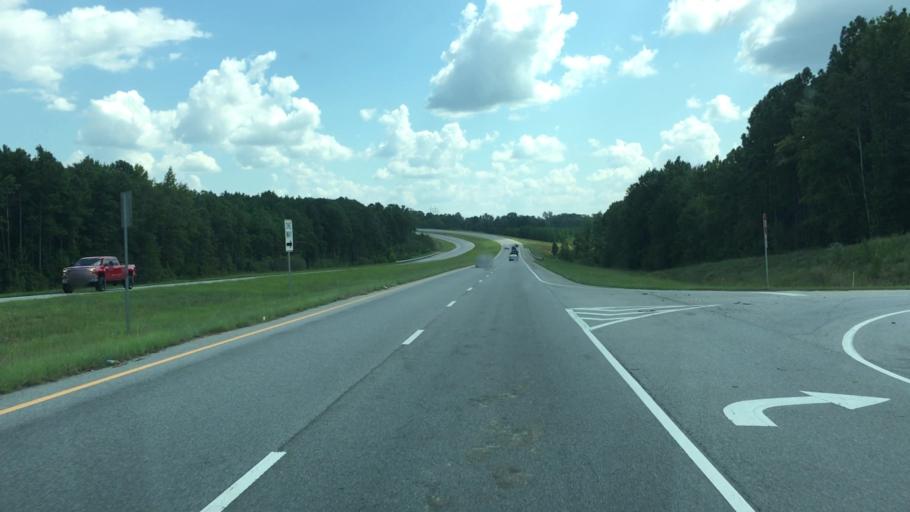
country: US
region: Georgia
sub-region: Putnam County
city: Eatonton
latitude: 33.2824
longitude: -83.3709
